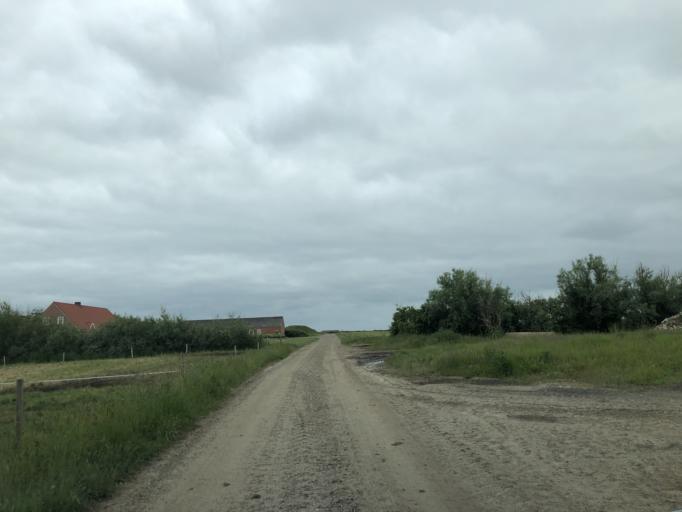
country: DK
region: Central Jutland
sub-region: Holstebro Kommune
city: Ulfborg
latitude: 56.2275
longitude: 8.1900
